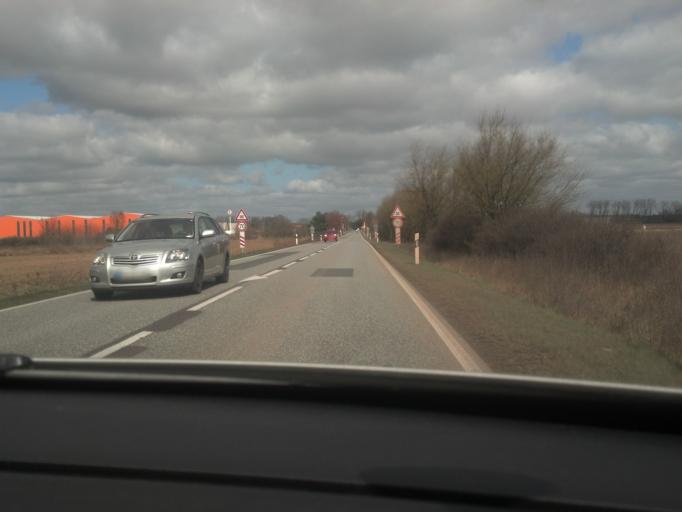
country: DE
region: Mecklenburg-Vorpommern
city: Plau am See
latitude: 53.3741
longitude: 12.2475
